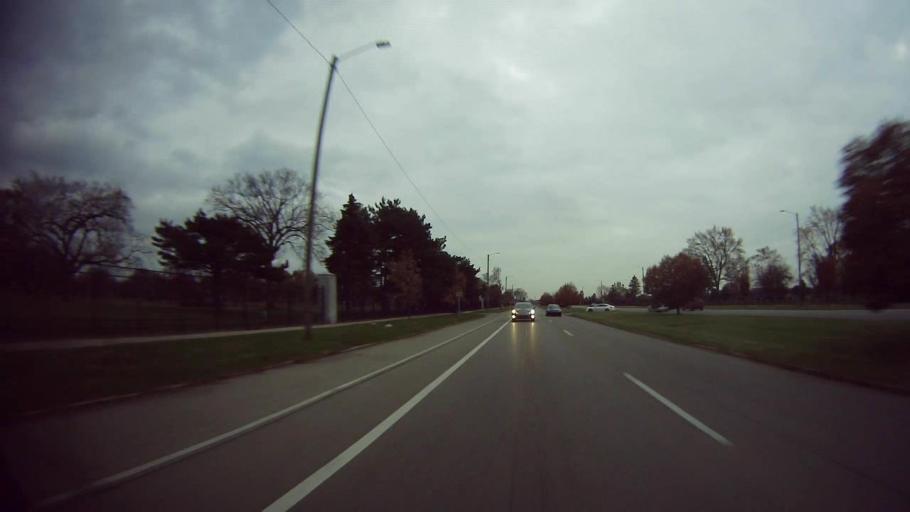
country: US
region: Michigan
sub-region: Wayne County
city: Hamtramck
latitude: 42.4239
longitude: -83.0139
